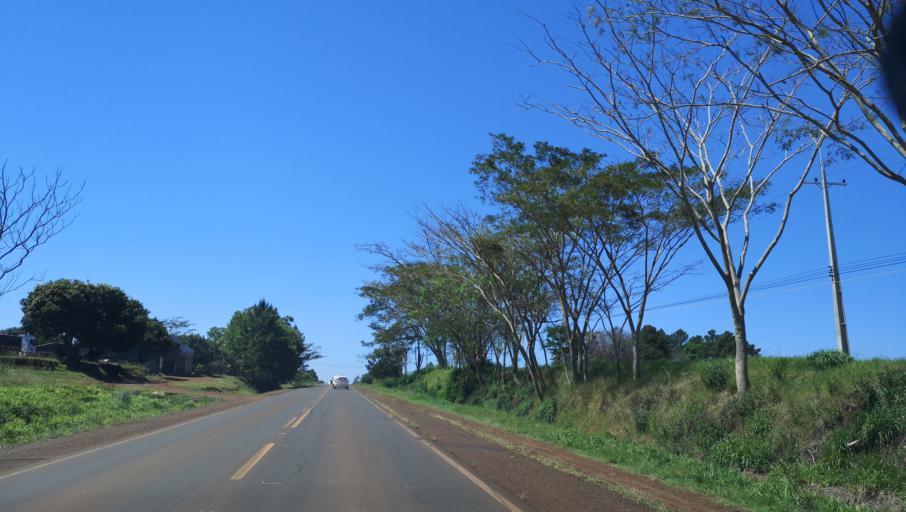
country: PY
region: Itapua
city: San Juan del Parana
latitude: -27.2609
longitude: -55.9652
